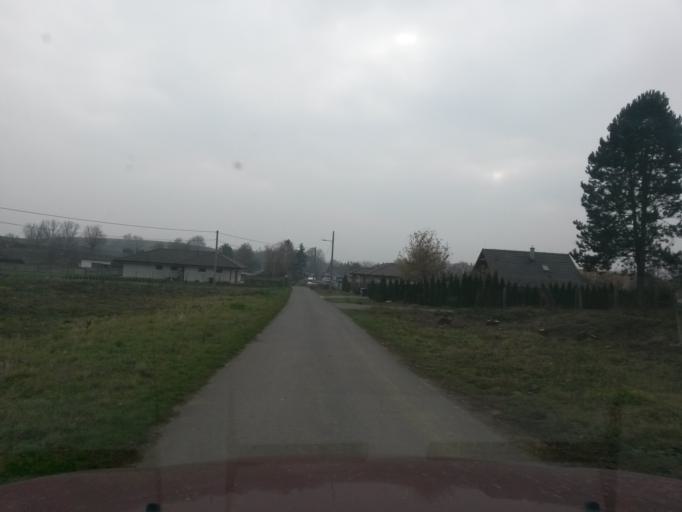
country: SK
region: Presovsky
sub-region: Okres Presov
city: Presov
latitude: 48.8800
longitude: 21.2730
